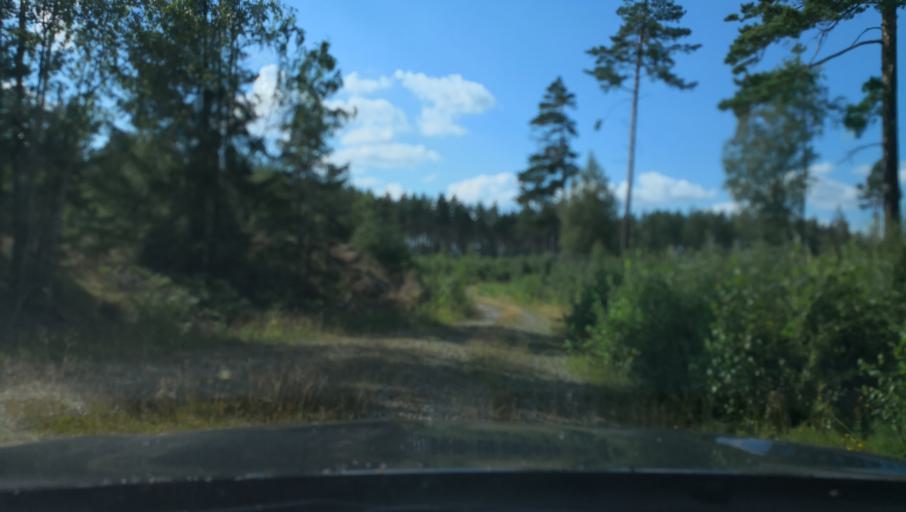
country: SE
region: Vaestmanland
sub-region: Vasteras
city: Skultuna
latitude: 59.7159
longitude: 16.3883
